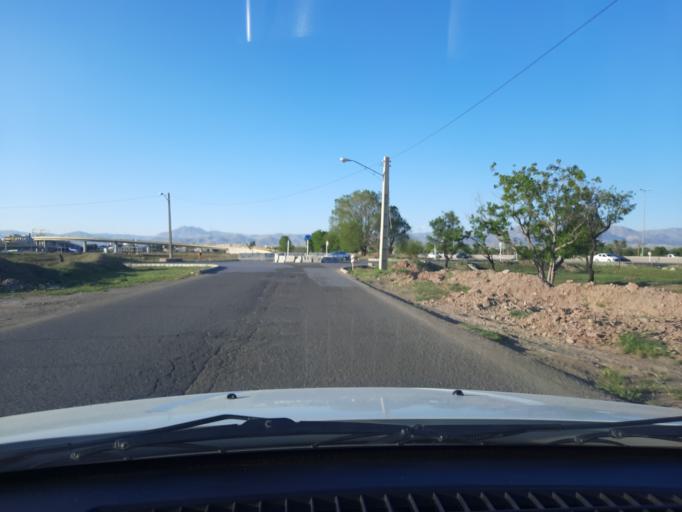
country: IR
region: Qazvin
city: Qazvin
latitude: 36.2689
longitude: 50.0252
